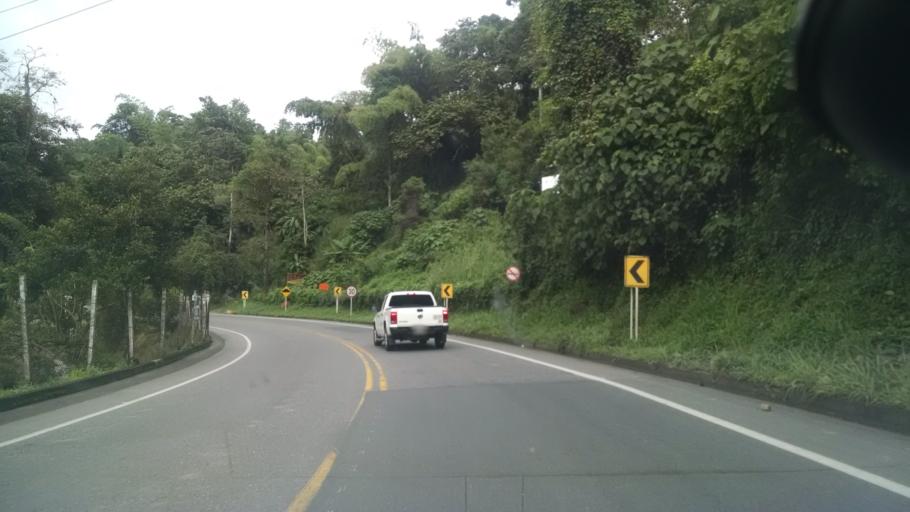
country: CO
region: Caldas
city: Palestina
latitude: 5.0703
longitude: -75.6213
